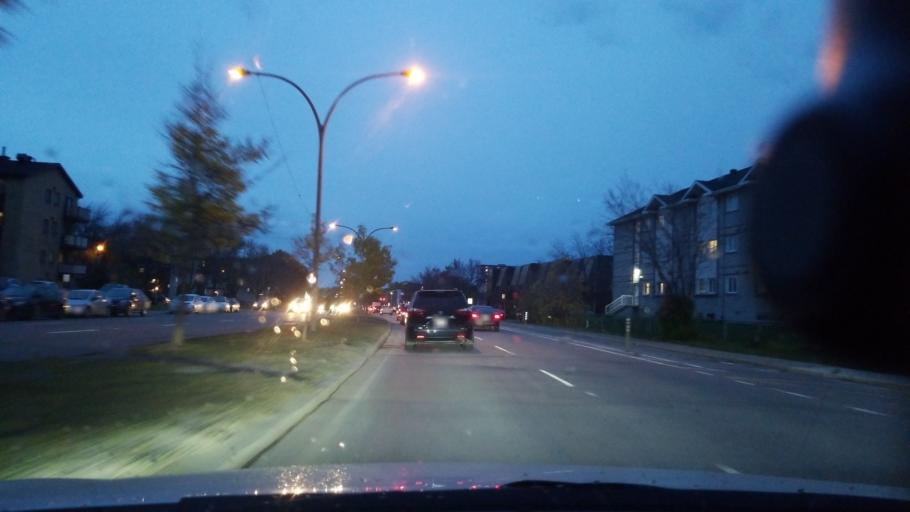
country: CA
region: Quebec
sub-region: Laval
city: Laval
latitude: 45.5625
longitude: -73.7205
